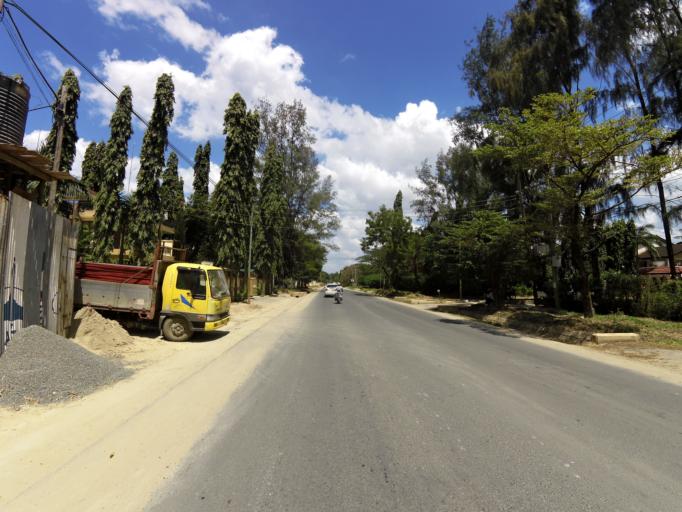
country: TZ
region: Dar es Salaam
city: Magomeni
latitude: -6.7671
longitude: 39.2497
